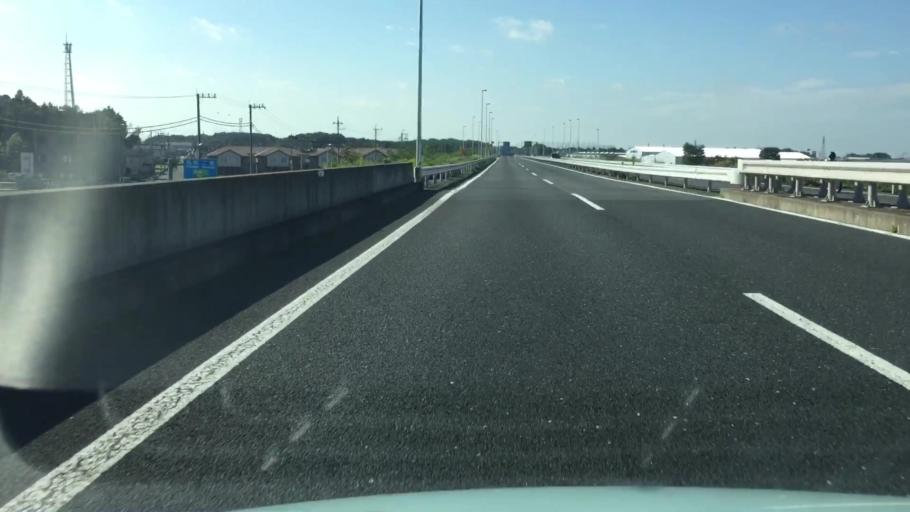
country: JP
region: Tochigi
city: Mooka
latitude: 36.4566
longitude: 139.9788
